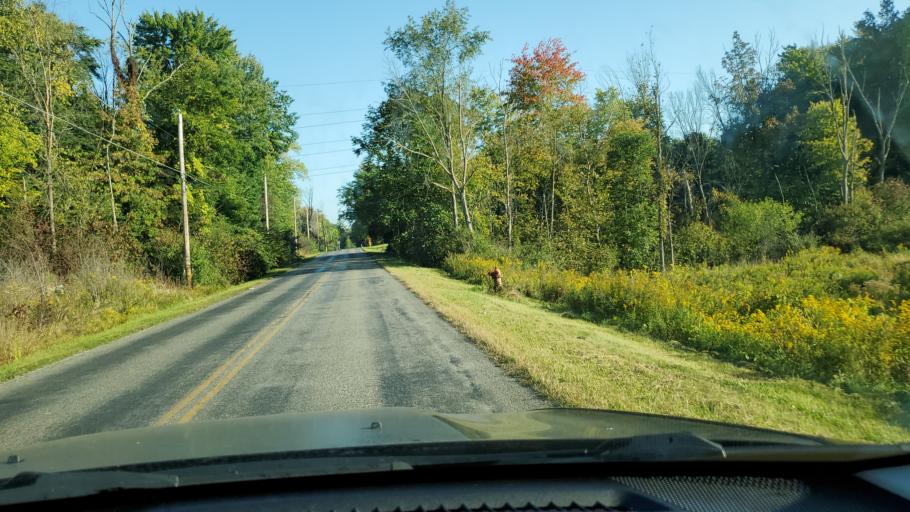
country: US
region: Ohio
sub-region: Trumbull County
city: Niles
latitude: 41.1625
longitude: -80.7535
